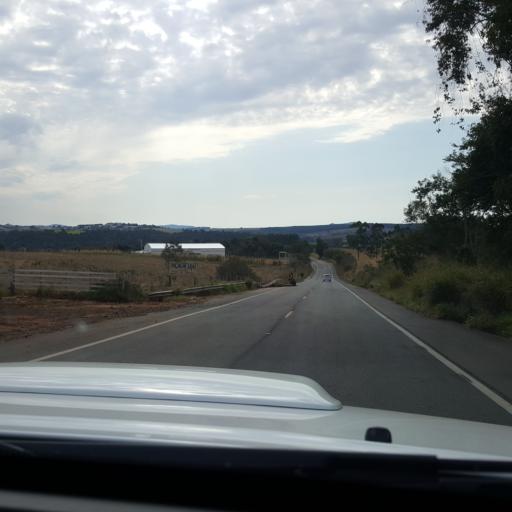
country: BR
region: Sao Paulo
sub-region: Itaporanga
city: Itaporanga
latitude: -23.7316
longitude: -49.4585
